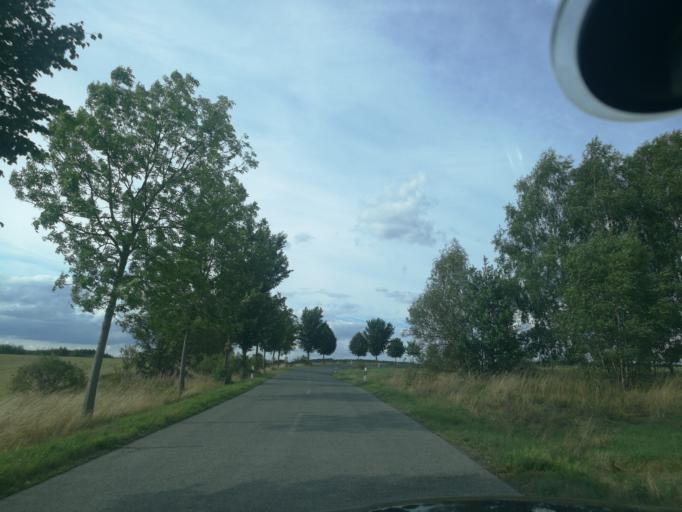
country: DE
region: Bavaria
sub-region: Upper Franconia
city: Regnitzlosau
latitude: 50.3239
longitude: 12.0959
